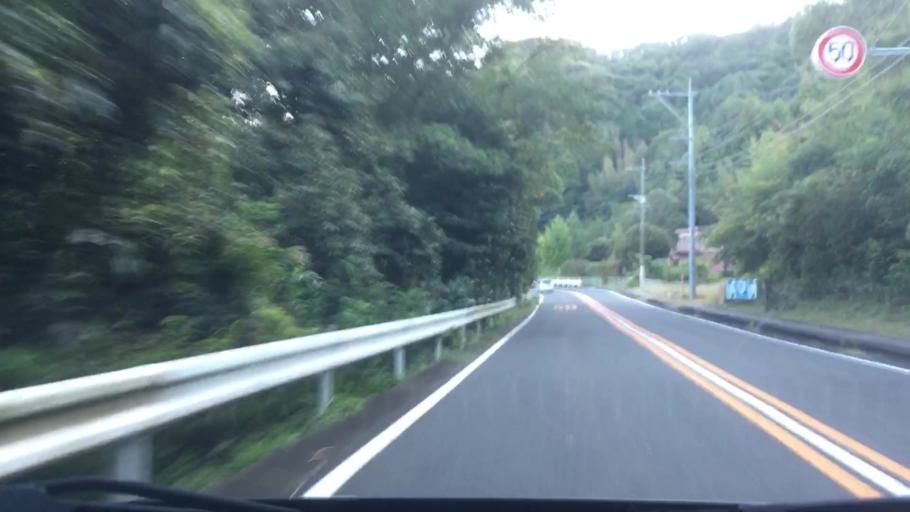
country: JP
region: Nagasaki
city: Sasebo
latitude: 33.0399
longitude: 129.7429
